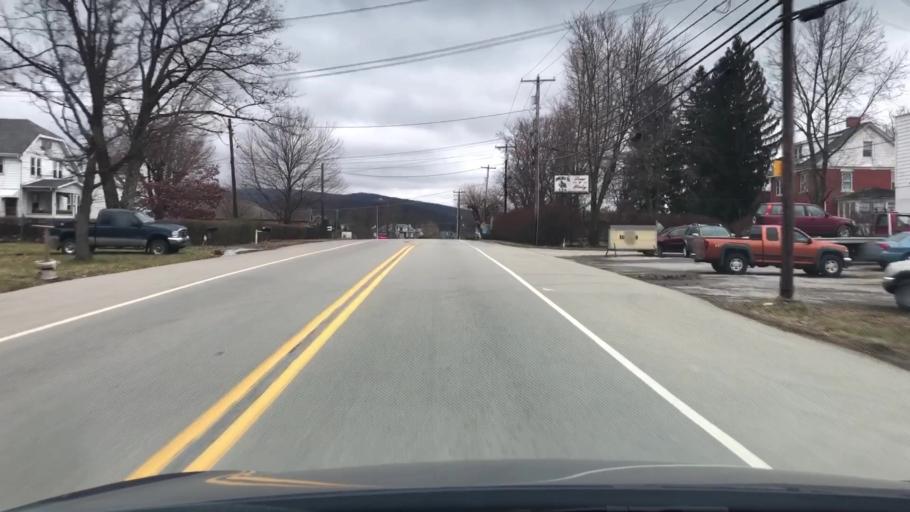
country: US
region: Pennsylvania
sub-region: Fayette County
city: Connellsville
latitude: 40.0285
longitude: -79.5811
